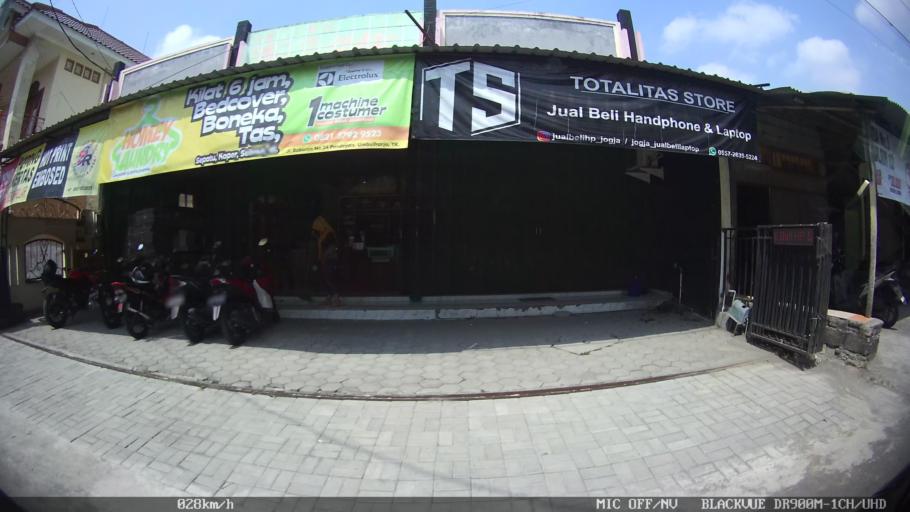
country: ID
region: Daerah Istimewa Yogyakarta
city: Yogyakarta
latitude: -7.8114
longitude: 110.3860
